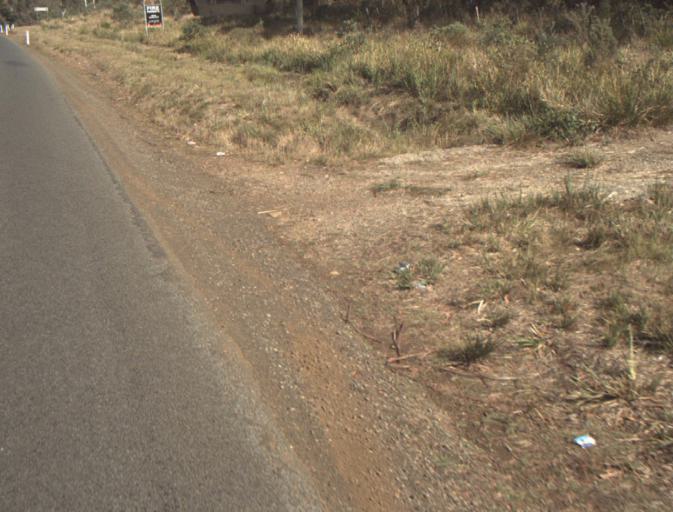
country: AU
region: Tasmania
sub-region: Launceston
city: Mayfield
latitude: -41.3378
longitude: 147.1433
